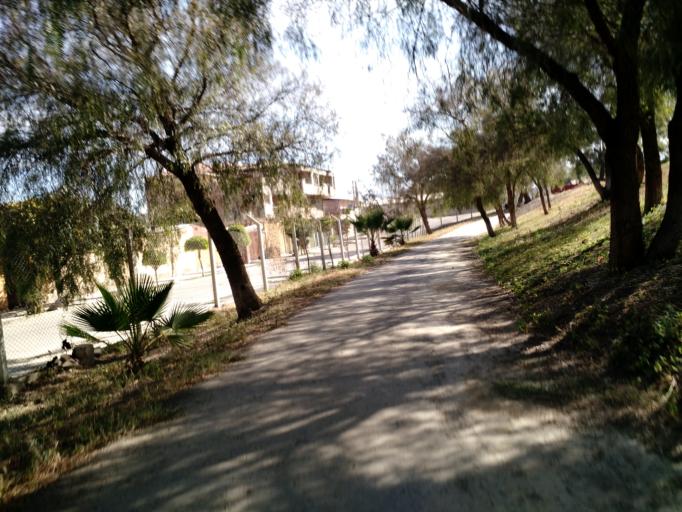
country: BO
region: Cochabamba
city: Cochabamba
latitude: -17.3897
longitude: -66.2070
